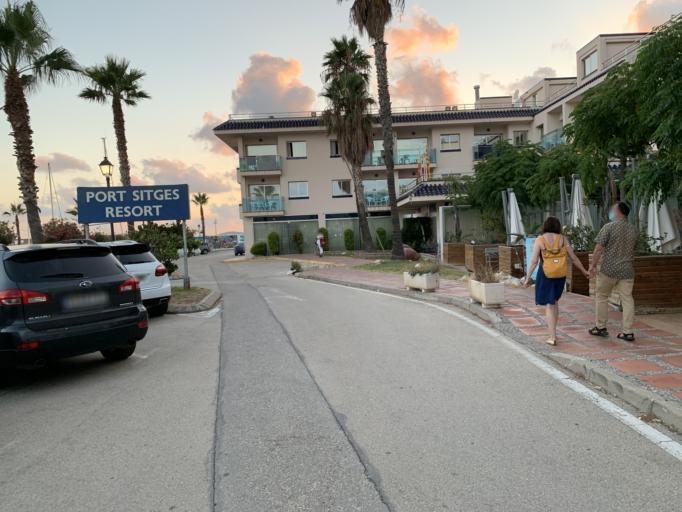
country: ES
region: Catalonia
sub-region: Provincia de Barcelona
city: Sitges
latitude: 41.2349
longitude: 1.8224
